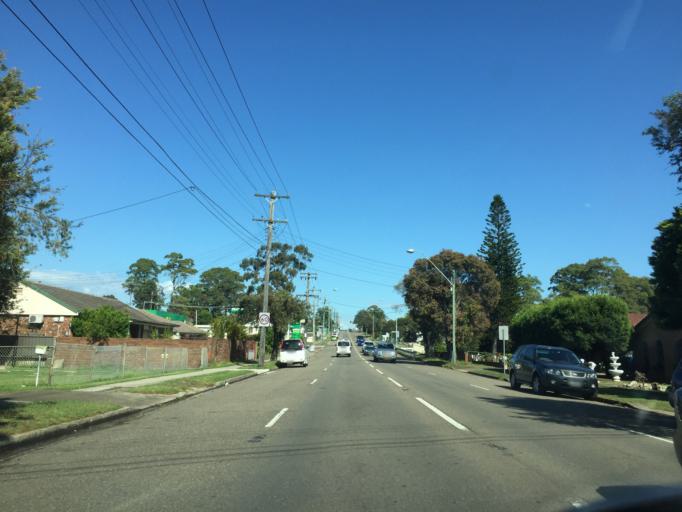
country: AU
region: New South Wales
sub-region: Fairfield
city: Fairfield Heights
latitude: -33.8515
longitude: 150.9267
